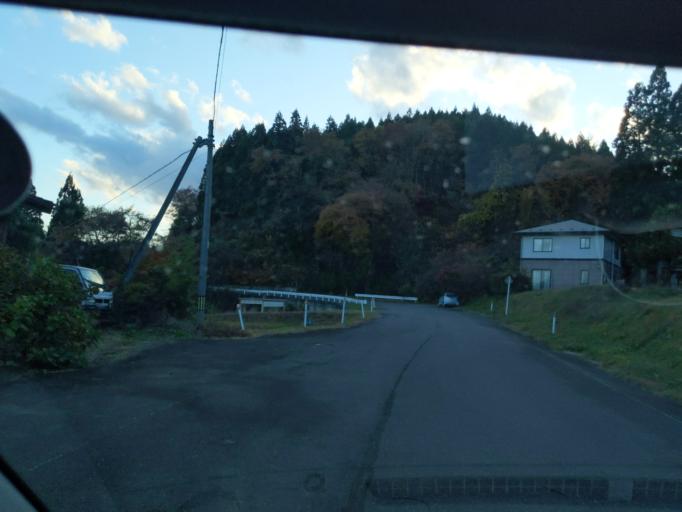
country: JP
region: Iwate
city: Mizusawa
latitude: 39.0303
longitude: 141.0382
